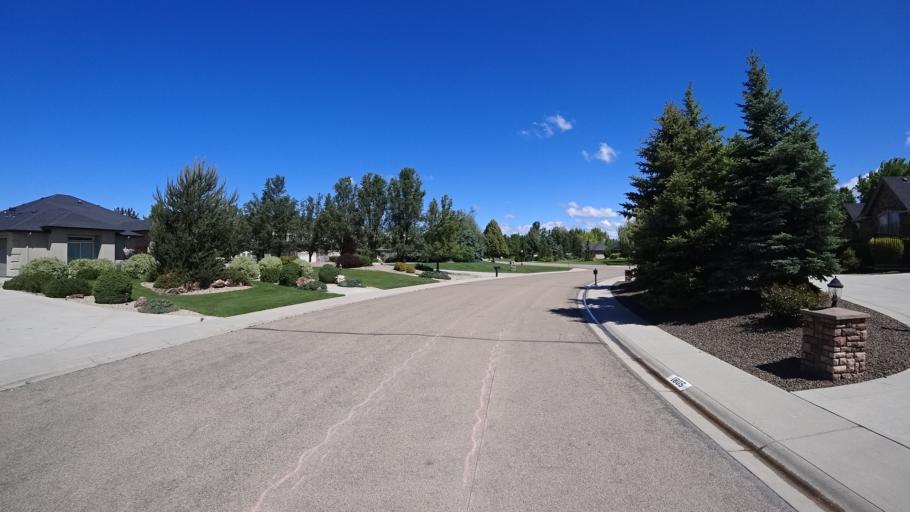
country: US
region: Idaho
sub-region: Ada County
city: Eagle
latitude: 43.6646
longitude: -116.3780
